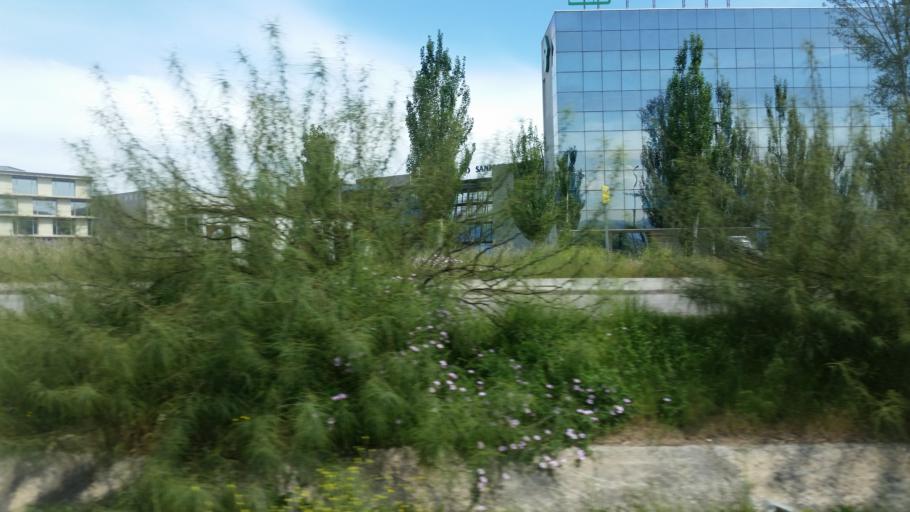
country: ES
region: Catalonia
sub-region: Provincia de Barcelona
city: El Prat de Llobregat
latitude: 41.3110
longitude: 2.0663
